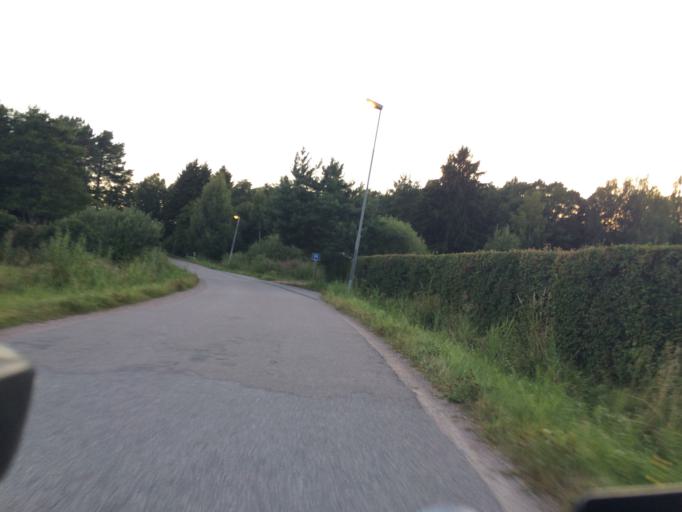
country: SE
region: Soedermanland
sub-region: Eskilstuna Kommun
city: Kvicksund
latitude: 59.4456
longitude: 16.3164
